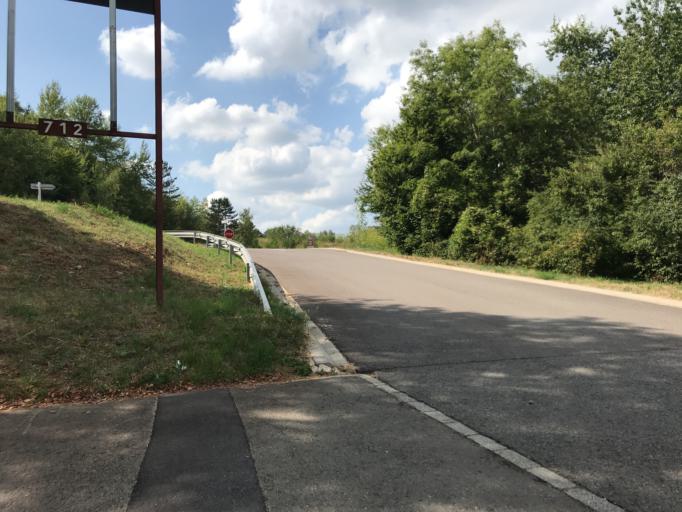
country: FR
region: Lorraine
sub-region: Departement de Meurthe-et-Moselle
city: Thil
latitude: 49.4920
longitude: 5.9120
